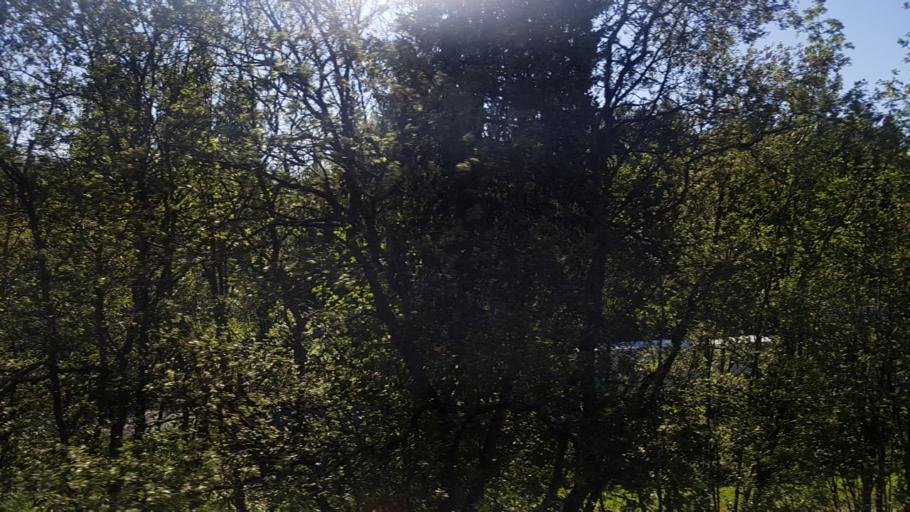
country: NO
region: Sor-Trondelag
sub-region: Trondheim
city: Trondheim
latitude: 63.3646
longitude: 10.3679
